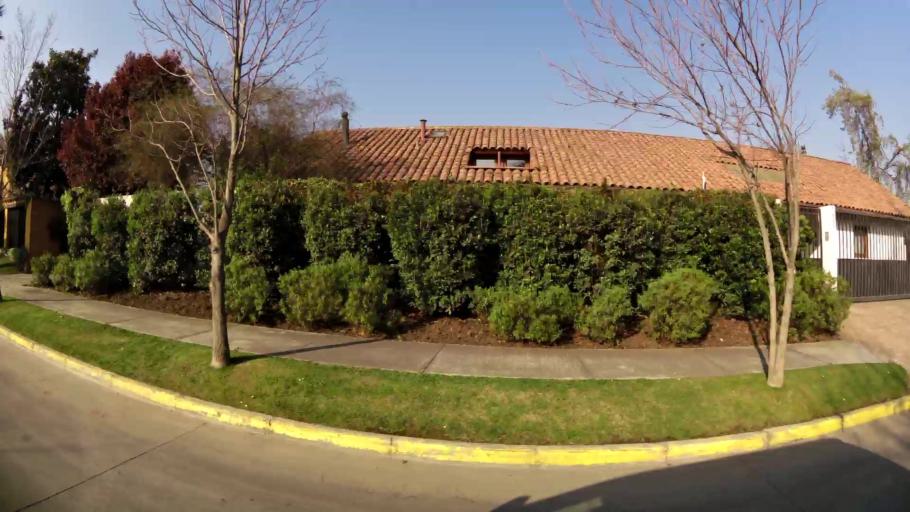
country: CL
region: Santiago Metropolitan
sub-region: Provincia de Santiago
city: Villa Presidente Frei, Nunoa, Santiago, Chile
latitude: -33.3595
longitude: -70.5337
